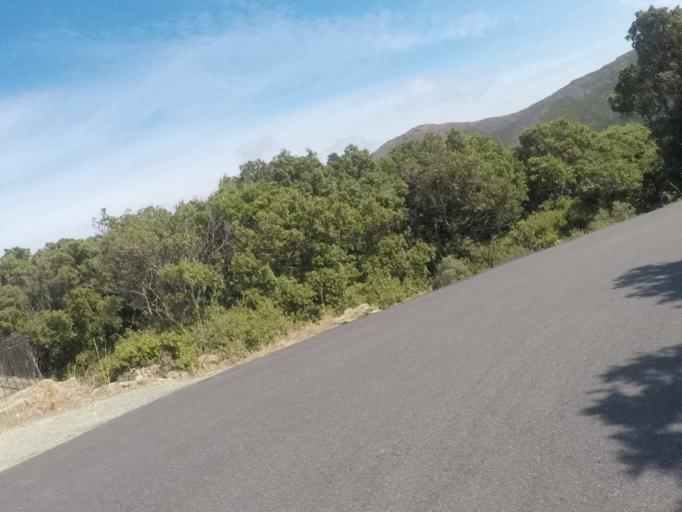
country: FR
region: Corsica
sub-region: Departement de la Haute-Corse
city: Brando
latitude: 42.9775
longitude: 9.3838
